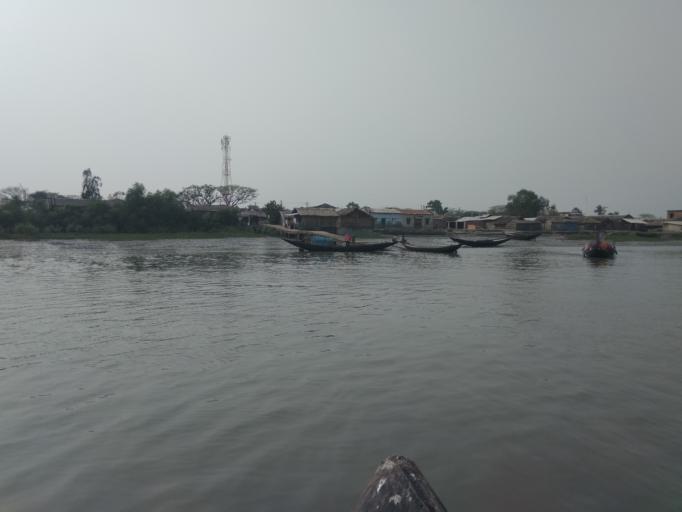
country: IN
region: West Bengal
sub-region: North 24 Parganas
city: Taki
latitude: 22.3470
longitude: 89.2041
